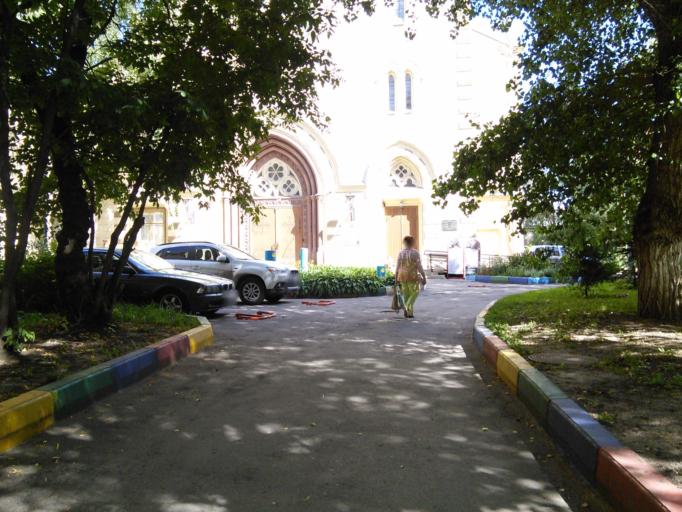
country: RU
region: Moscow
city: Zamoskvorech'ye
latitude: 55.7568
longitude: 37.6401
